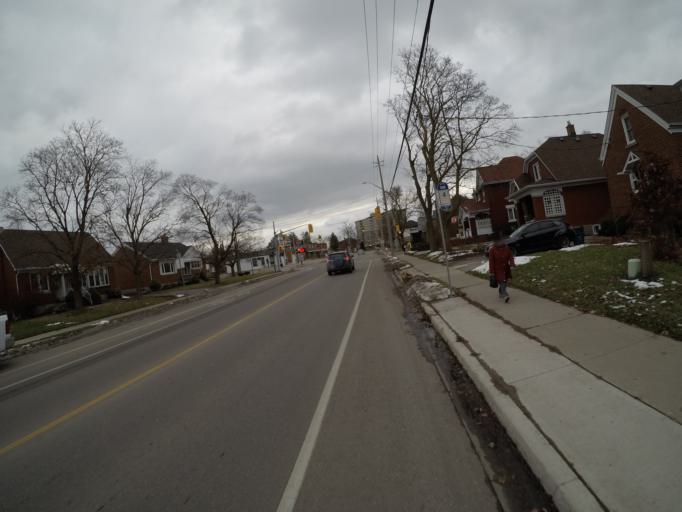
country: CA
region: Ontario
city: Waterloo
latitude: 43.4634
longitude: -80.4946
